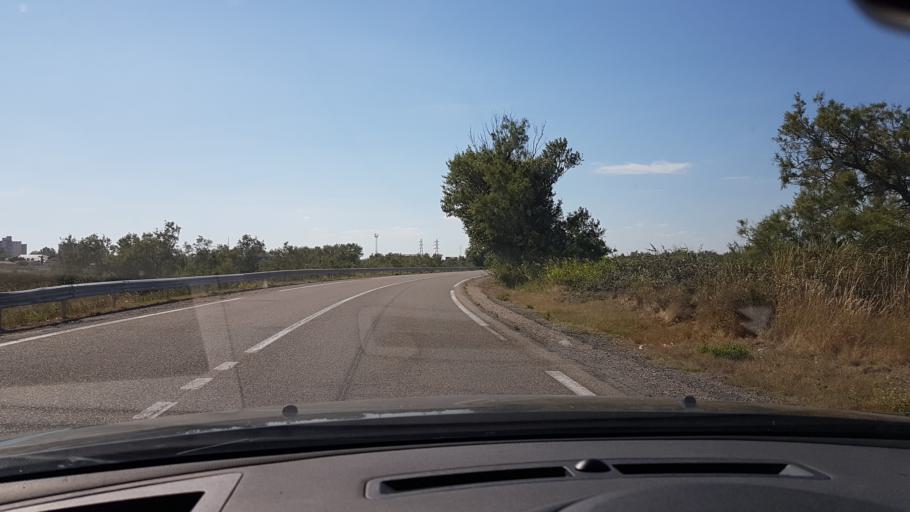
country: FR
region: Provence-Alpes-Cote d'Azur
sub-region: Departement des Bouches-du-Rhone
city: Port-Saint-Louis-du-Rhone
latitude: 43.3908
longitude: 4.8200
